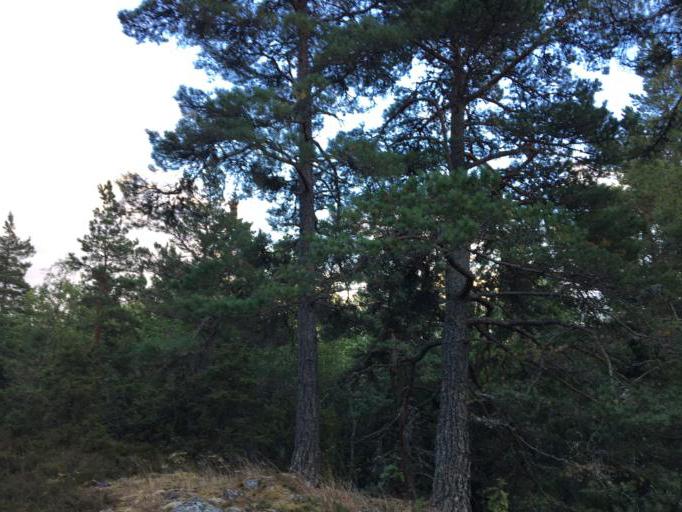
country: SE
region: Soedermanland
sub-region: Eskilstuna Kommun
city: Kvicksund
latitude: 59.4162
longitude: 16.3212
